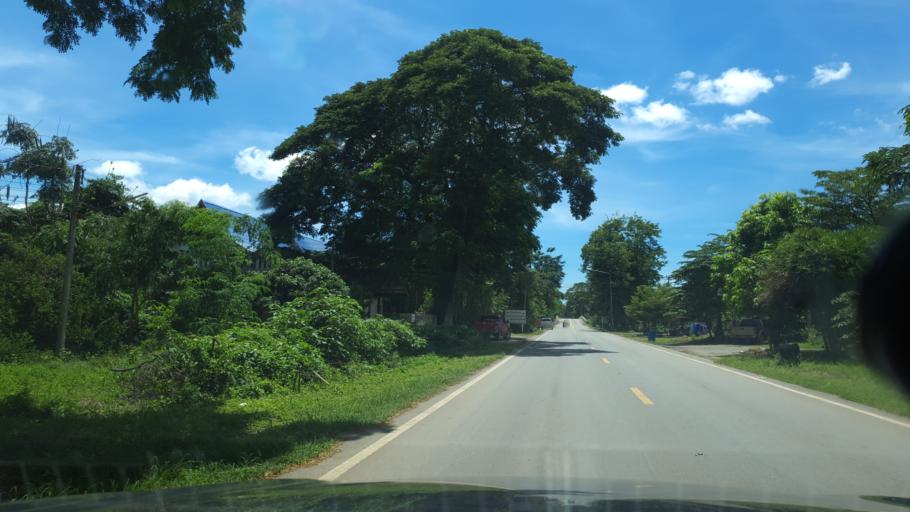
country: TH
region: Sukhothai
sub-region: Amphoe Si Satchanalai
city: Si Satchanalai
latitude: 17.4337
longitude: 99.8017
